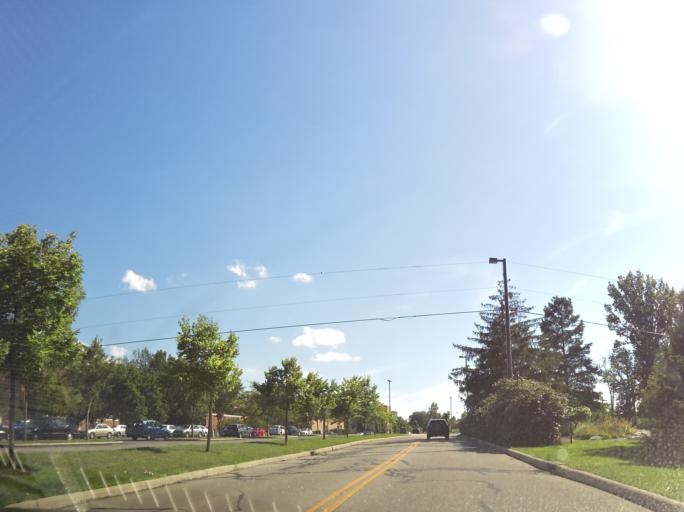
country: US
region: Ohio
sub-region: Greene County
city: Wright-Patterson AFB
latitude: 39.7852
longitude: -84.0638
